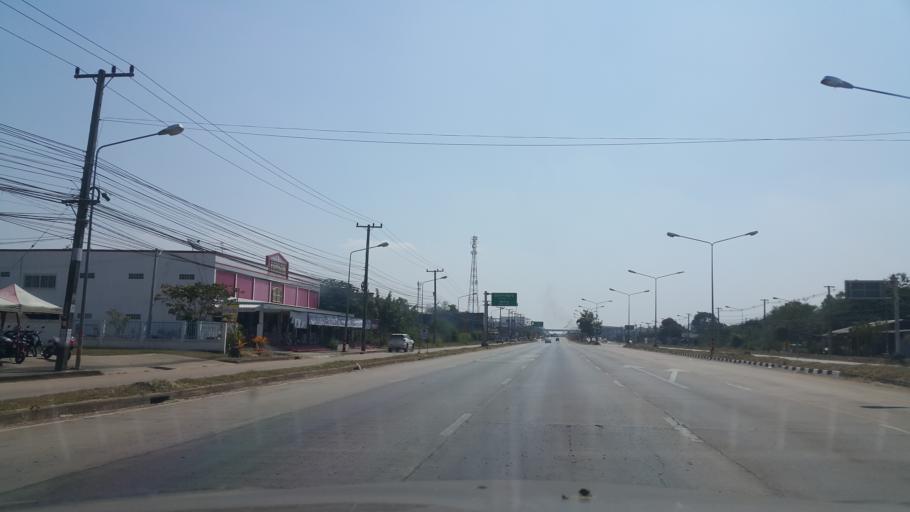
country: TH
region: Changwat Udon Thani
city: Non Sa-at
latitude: 16.9760
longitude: 102.8928
